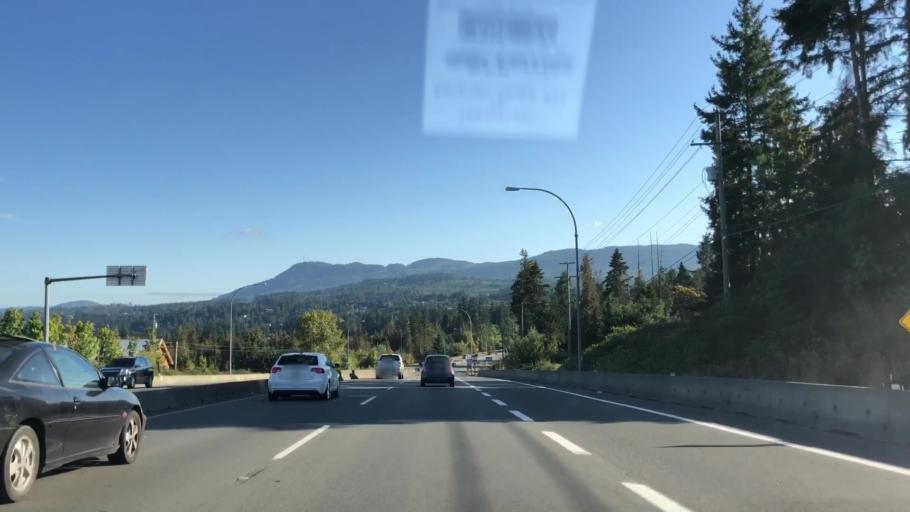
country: CA
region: British Columbia
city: North Saanich
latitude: 48.6644
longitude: -123.5596
